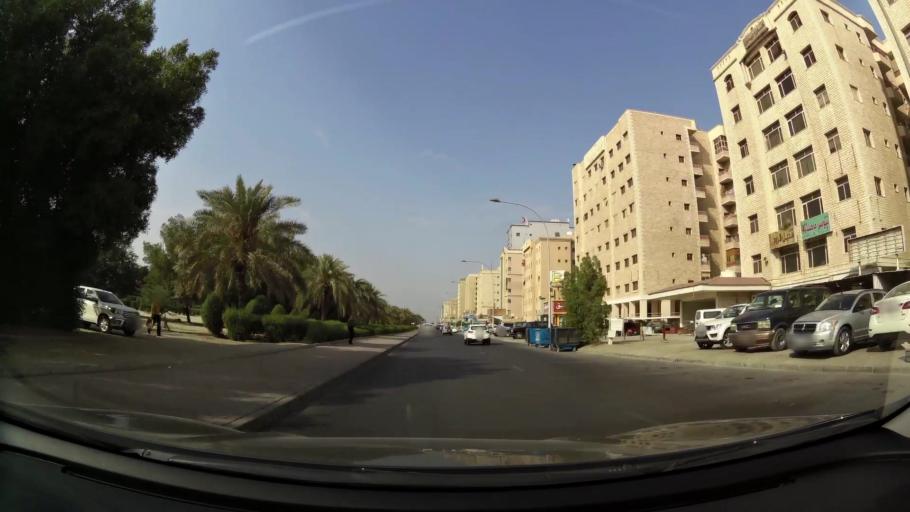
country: KW
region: Al Farwaniyah
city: Al Farwaniyah
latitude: 29.2877
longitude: 47.9673
